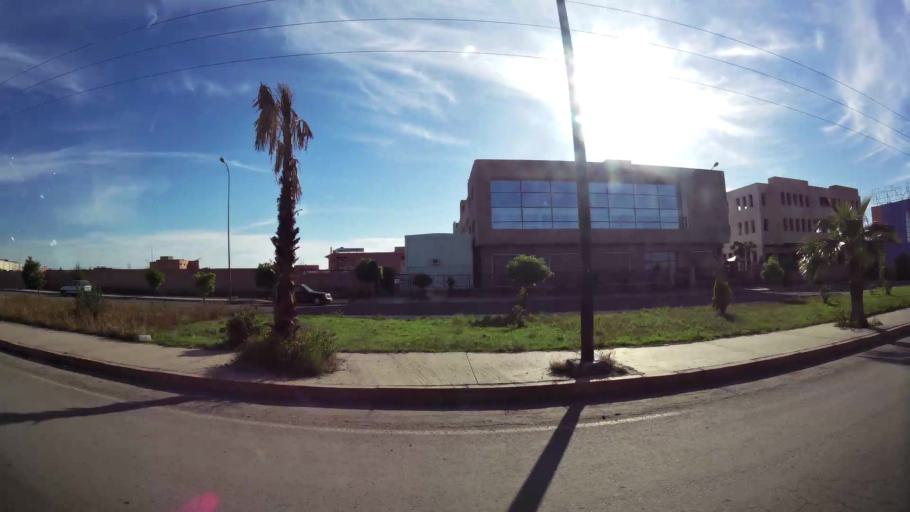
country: MA
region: Marrakech-Tensift-Al Haouz
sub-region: Marrakech
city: Marrakesh
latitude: 31.6876
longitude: -8.0533
